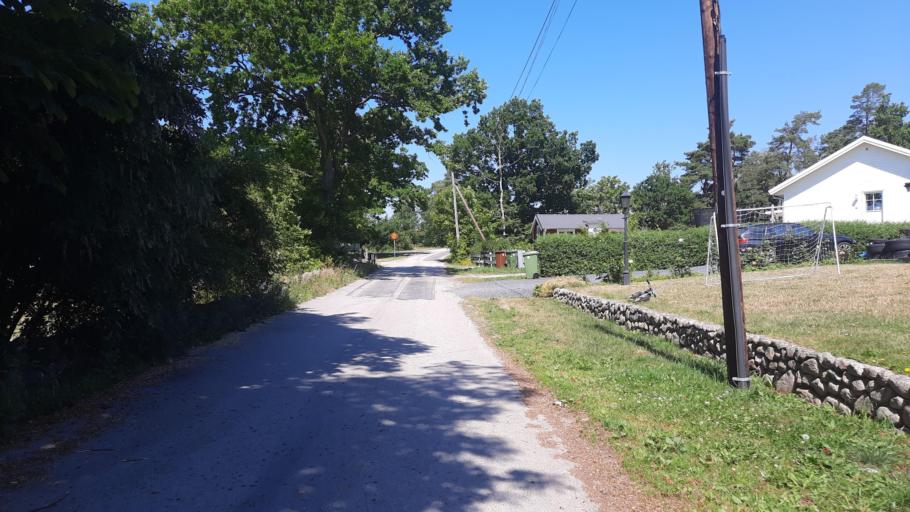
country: SE
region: Blekinge
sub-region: Karlskrona Kommun
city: Jaemjoe
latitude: 56.1472
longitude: 15.7710
